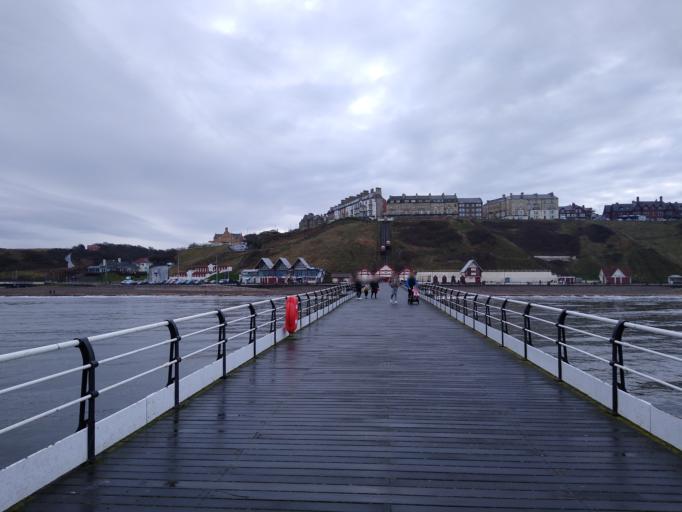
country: GB
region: England
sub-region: Redcar and Cleveland
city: Saltburn-by-the-Sea
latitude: 54.5881
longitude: -0.9696
